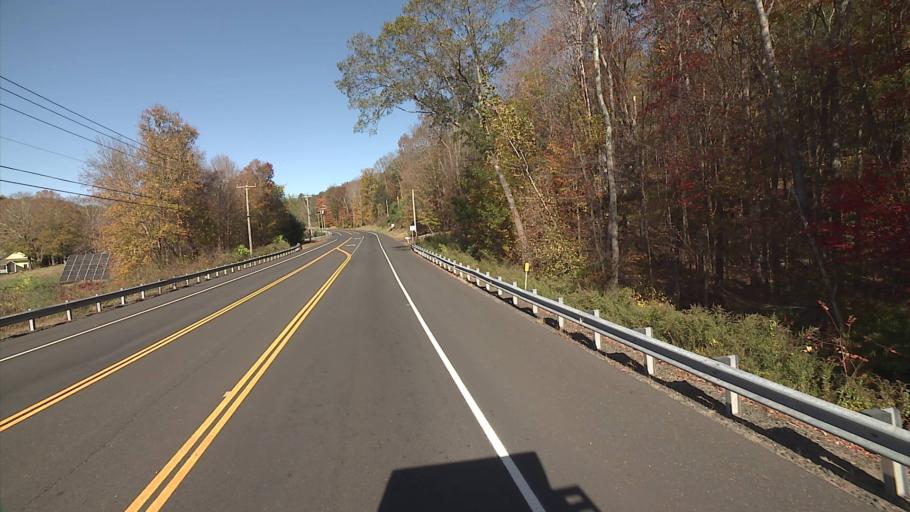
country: US
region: Connecticut
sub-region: Tolland County
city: Coventry Lake
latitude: 41.7809
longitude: -72.4219
